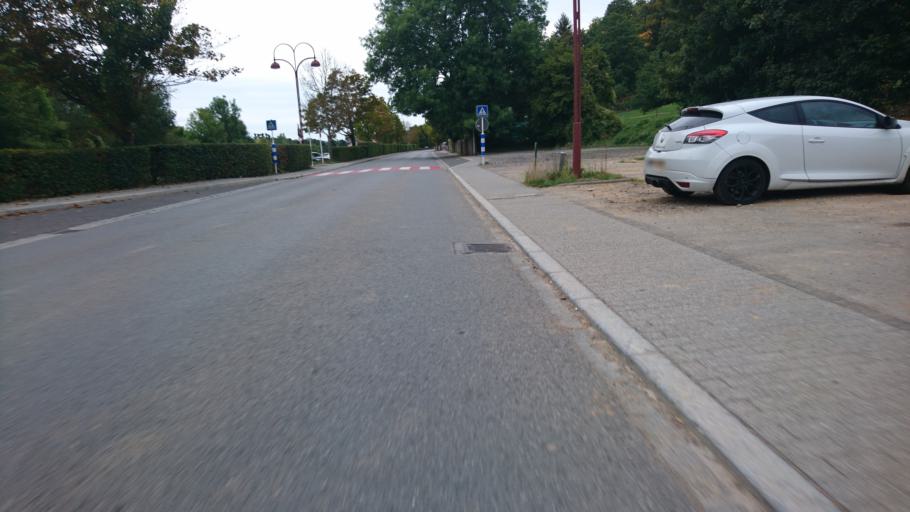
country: LU
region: Luxembourg
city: Colmar
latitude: 49.8056
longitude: 6.0923
